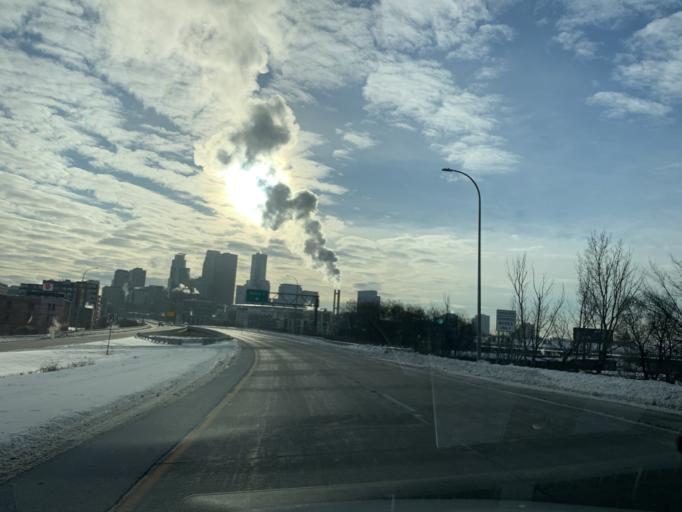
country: US
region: Minnesota
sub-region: Hennepin County
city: Minneapolis
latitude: 44.9895
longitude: -93.2841
